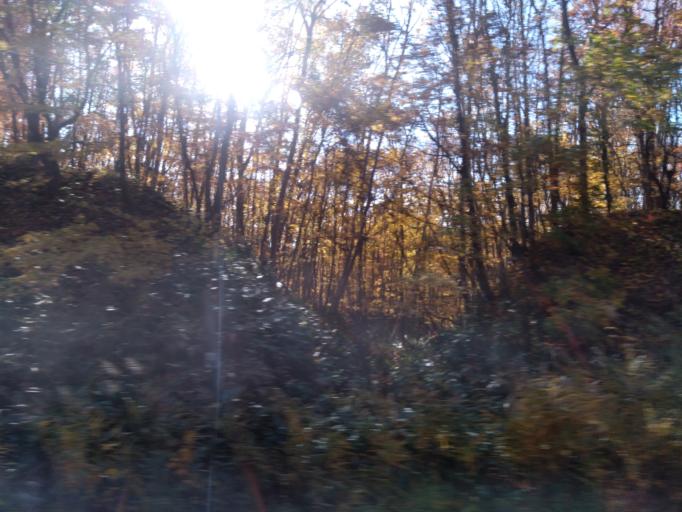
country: JP
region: Hokkaido
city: Kitahiroshima
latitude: 43.0103
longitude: 141.4955
